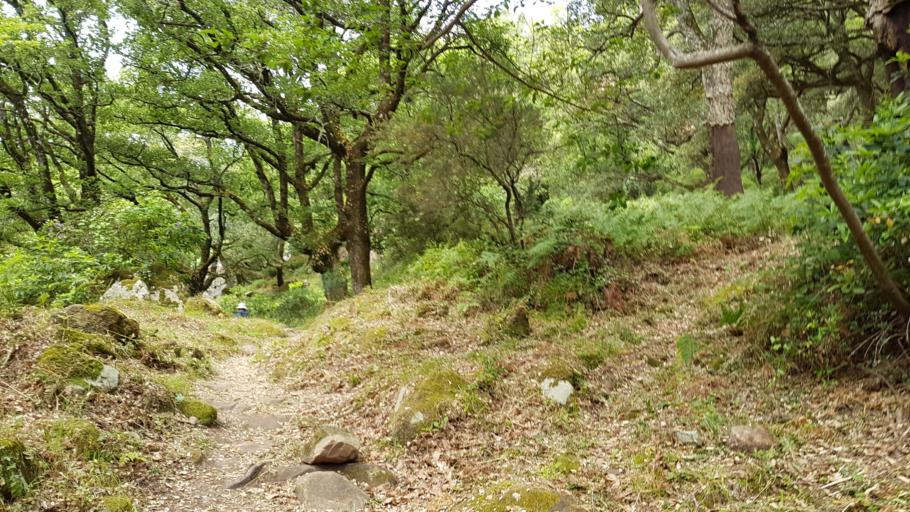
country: ES
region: Andalusia
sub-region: Provincia de Cadiz
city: Alcala de los Gazules
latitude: 36.5184
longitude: -5.5936
